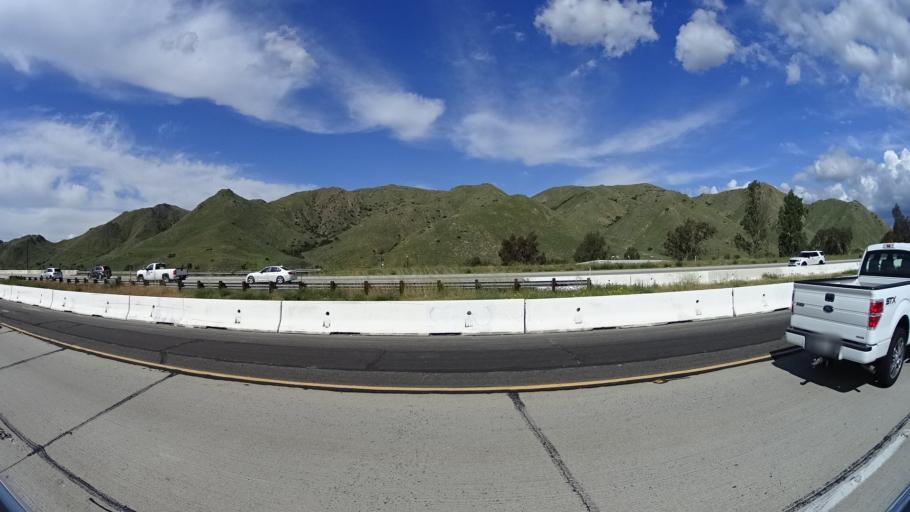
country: US
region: California
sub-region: Riverside County
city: Lake Elsinore
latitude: 33.7410
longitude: -117.4319
